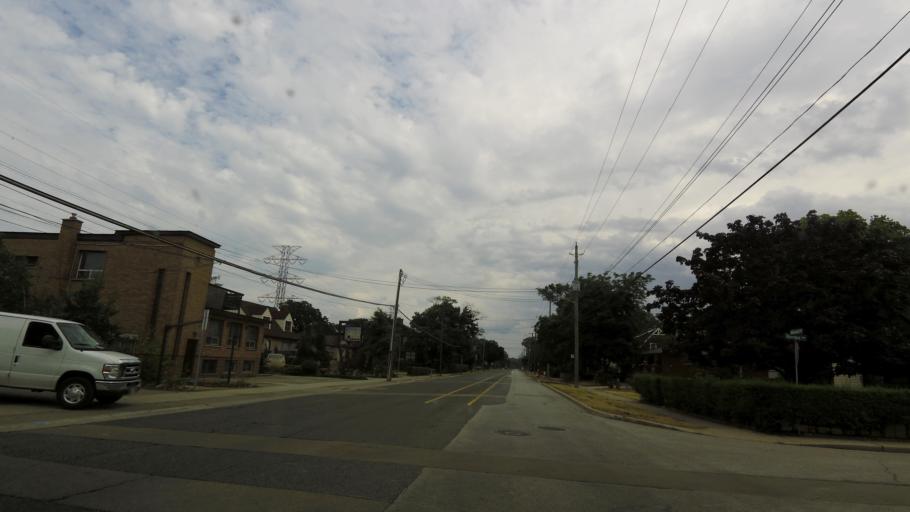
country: CA
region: Ontario
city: Hamilton
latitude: 43.2829
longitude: -79.7863
